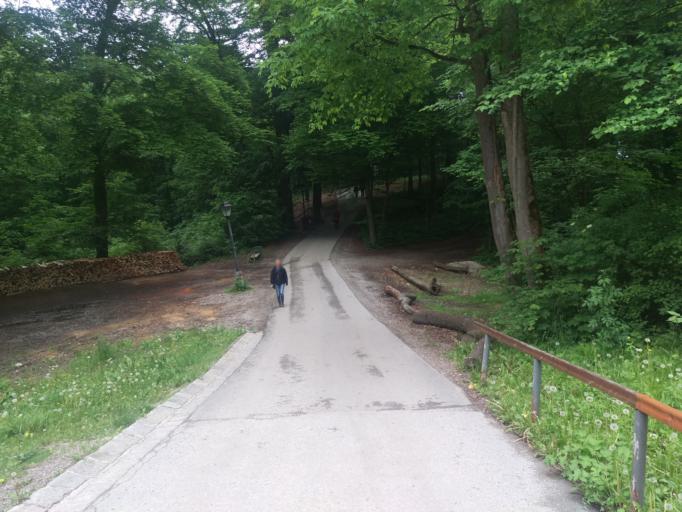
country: AT
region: Salzburg
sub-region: Salzburg Stadt
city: Salzburg
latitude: 47.7991
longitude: 13.0386
